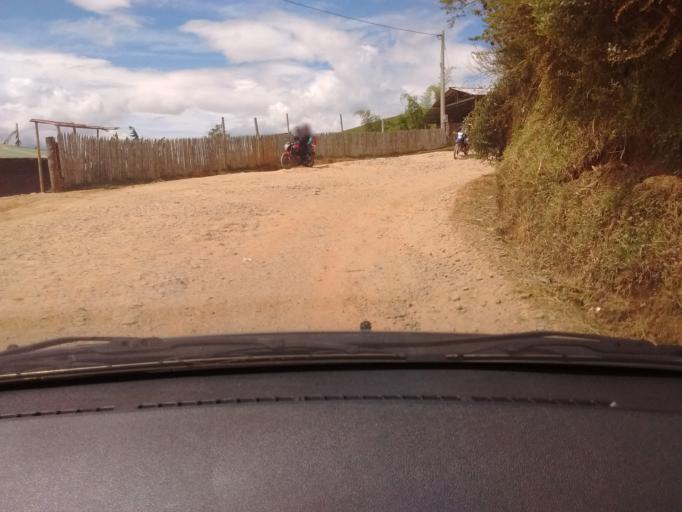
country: CO
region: Cauca
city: El Tambo
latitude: 2.4468
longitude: -76.8173
